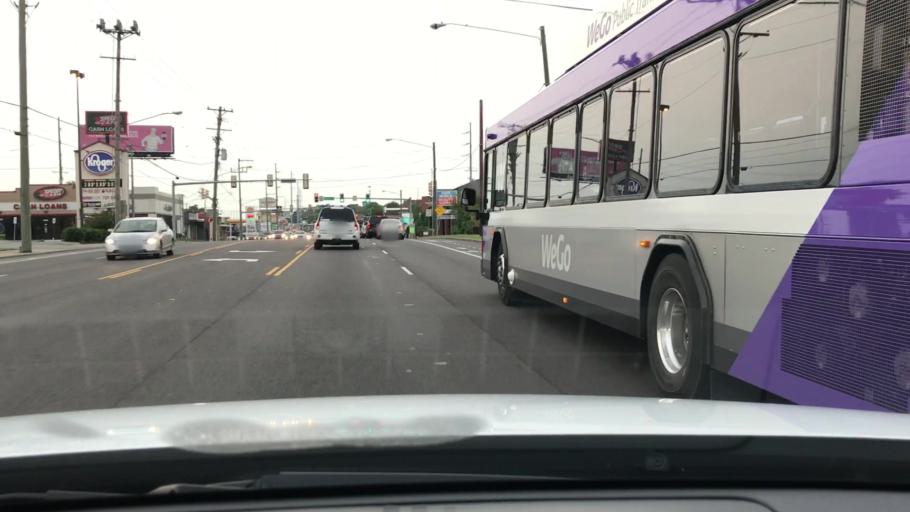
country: US
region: Tennessee
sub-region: Davidson County
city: Goodlettsville
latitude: 36.2613
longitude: -86.7125
